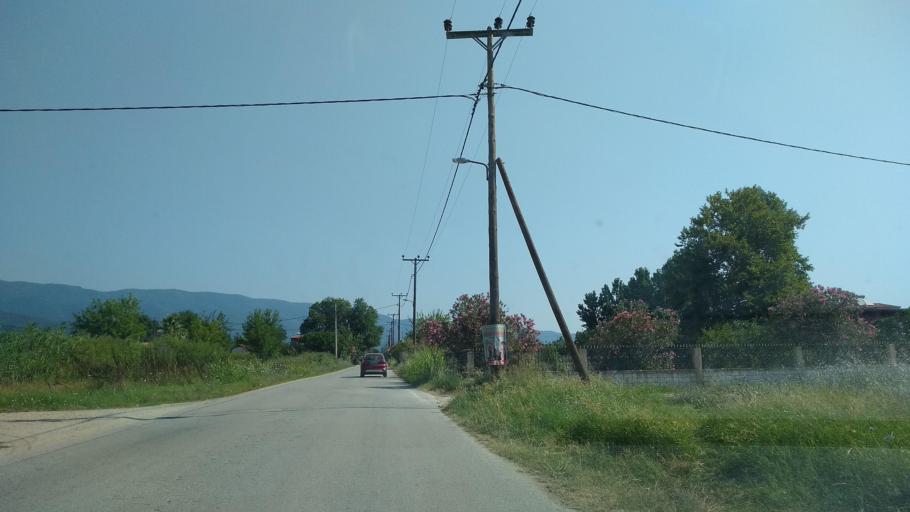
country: GR
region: Central Macedonia
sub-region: Nomos Thessalonikis
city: Stavros
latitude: 40.6829
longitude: 23.6876
